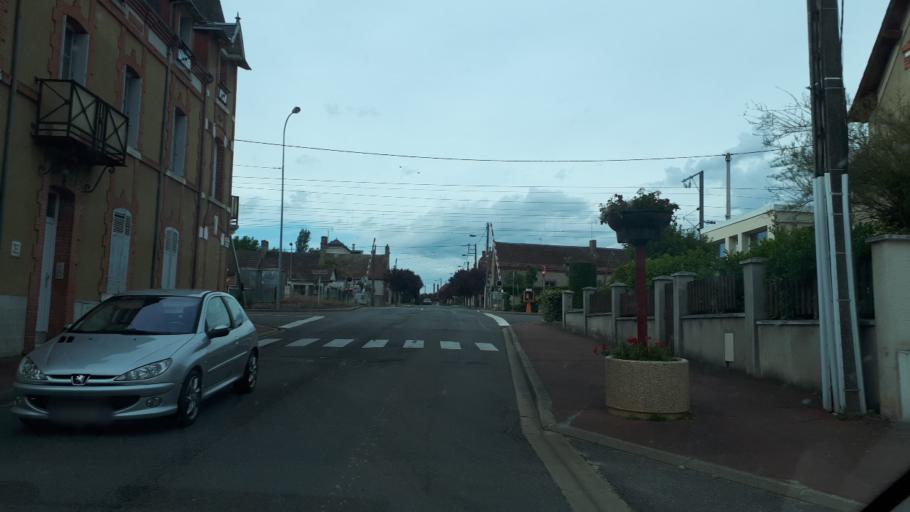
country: FR
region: Centre
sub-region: Departement du Loir-et-Cher
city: Villefranche-sur-Cher
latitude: 47.2942
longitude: 1.7697
